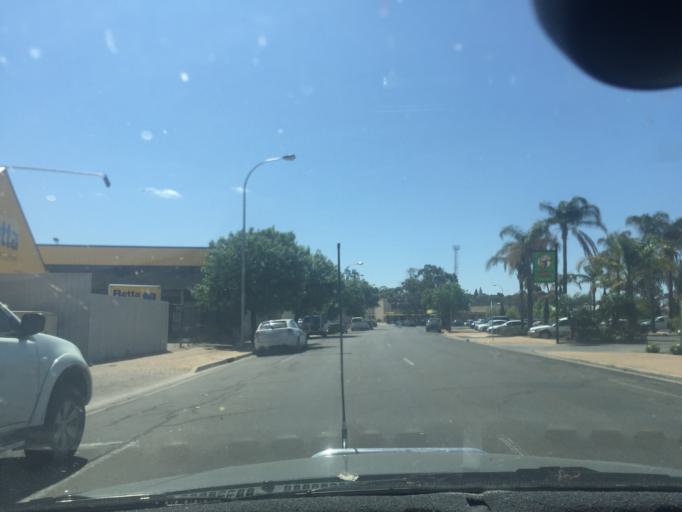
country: AU
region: South Australia
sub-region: Berri and Barmera
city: Berri
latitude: -34.2873
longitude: 140.6035
